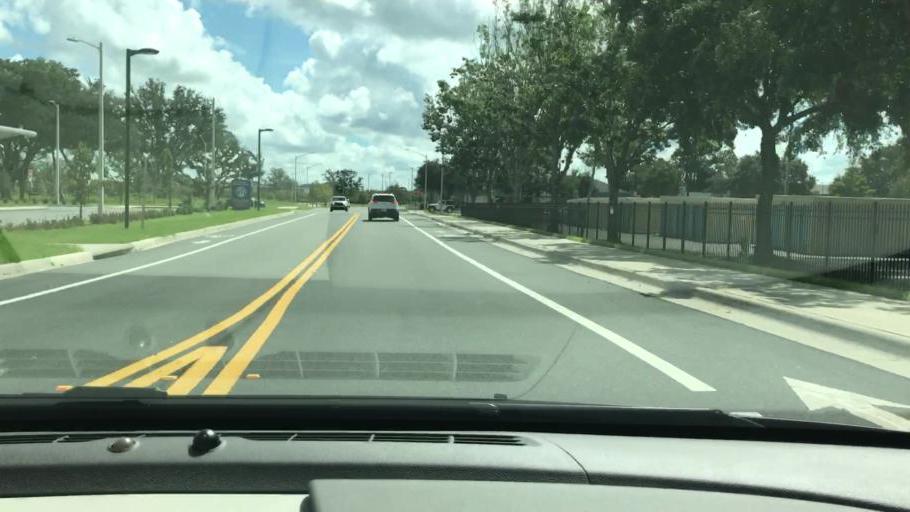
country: US
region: Florida
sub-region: Alachua County
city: Gainesville
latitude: 29.6252
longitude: -82.3880
